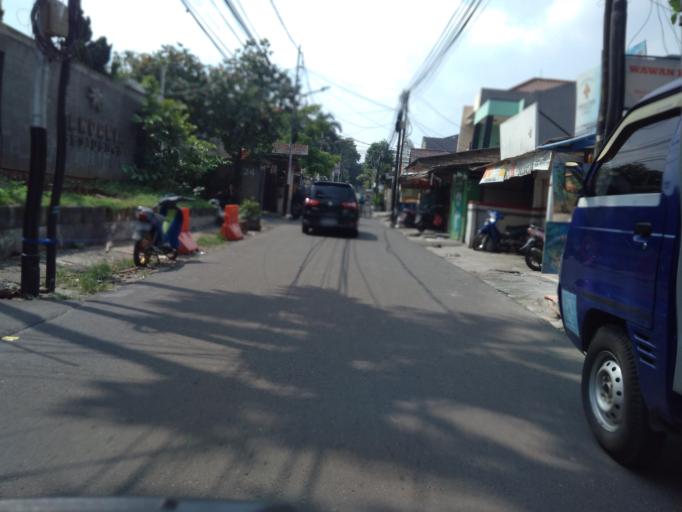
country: ID
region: Jakarta Raya
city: Jakarta
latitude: -6.2609
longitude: 106.7945
